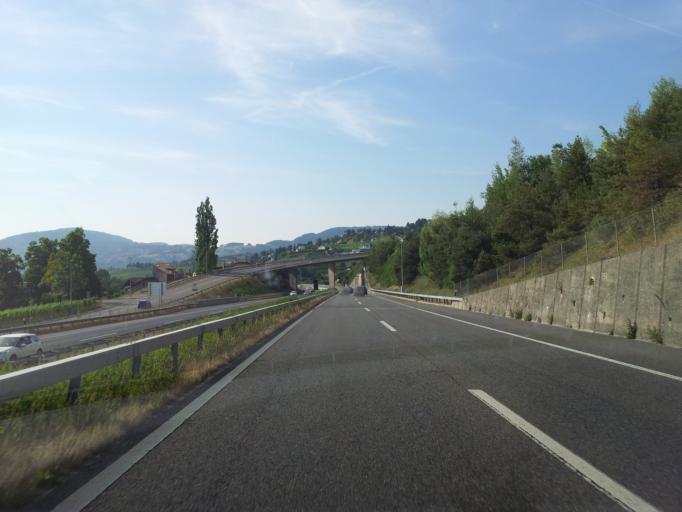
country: CH
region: Vaud
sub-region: Riviera-Pays-d'Enhaut District
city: Le Chatelard
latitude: 46.4480
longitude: 6.9015
